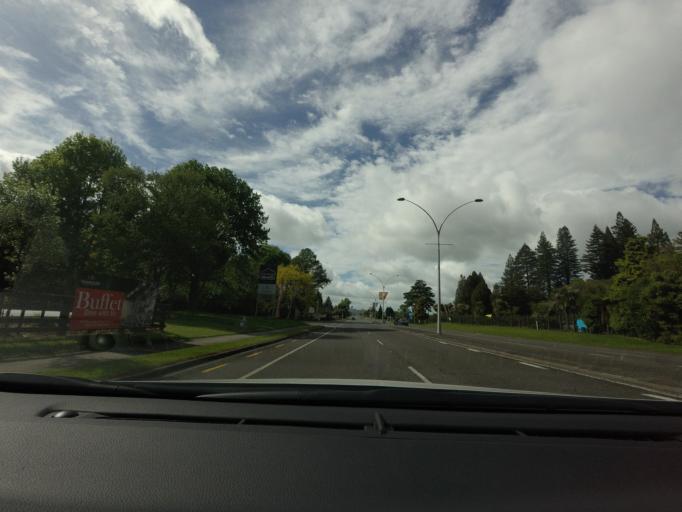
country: NZ
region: Bay of Plenty
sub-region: Rotorua District
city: Rotorua
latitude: -38.1082
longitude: 176.2223
